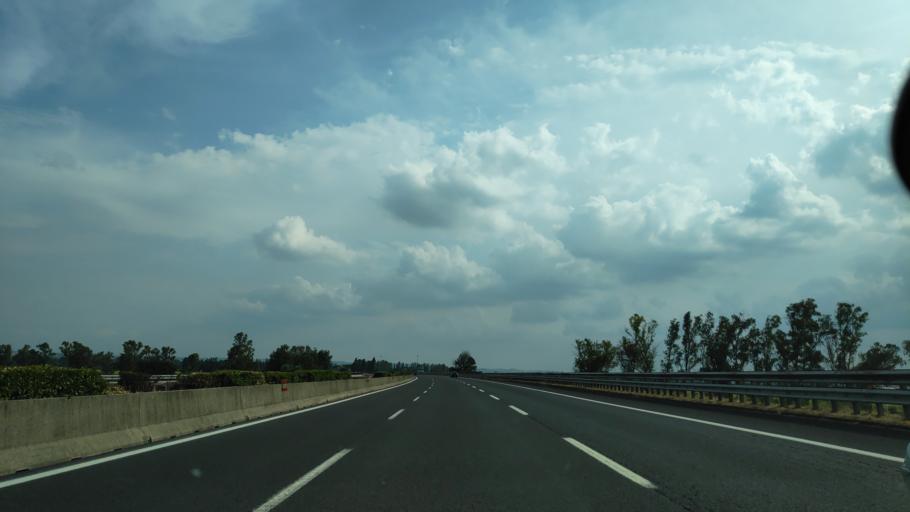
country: IT
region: Latium
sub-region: Citta metropolitana di Roma Capitale
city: Bivio di Capanelle
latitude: 42.1334
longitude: 12.6178
